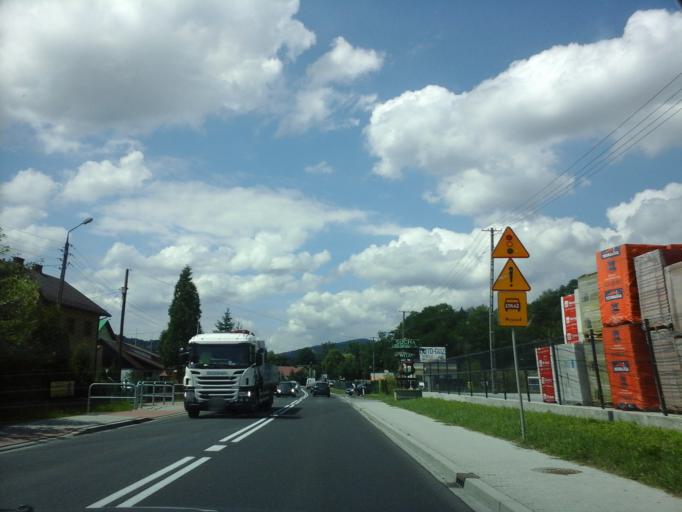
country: PL
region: Lesser Poland Voivodeship
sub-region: Powiat suski
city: Sucha Beskidzka
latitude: 49.7353
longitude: 19.6212
